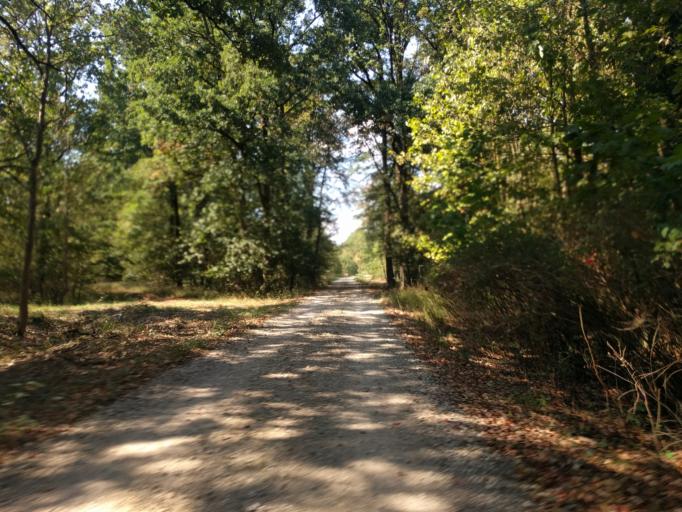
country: DE
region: Bavaria
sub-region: Upper Palatinate
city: Mintraching
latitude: 48.9868
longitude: 12.2734
